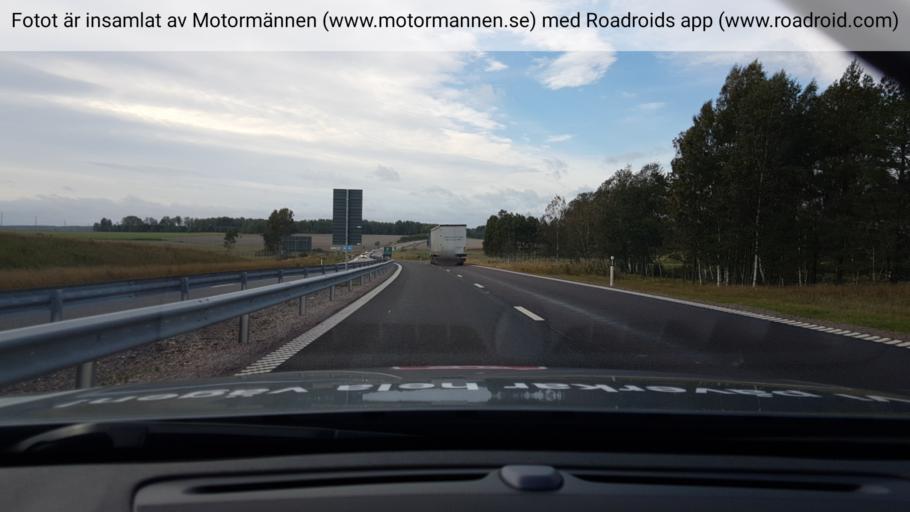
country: SE
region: Vaermland
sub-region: Karlstads Kommun
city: Edsvalla
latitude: 59.3920
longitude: 13.2738
